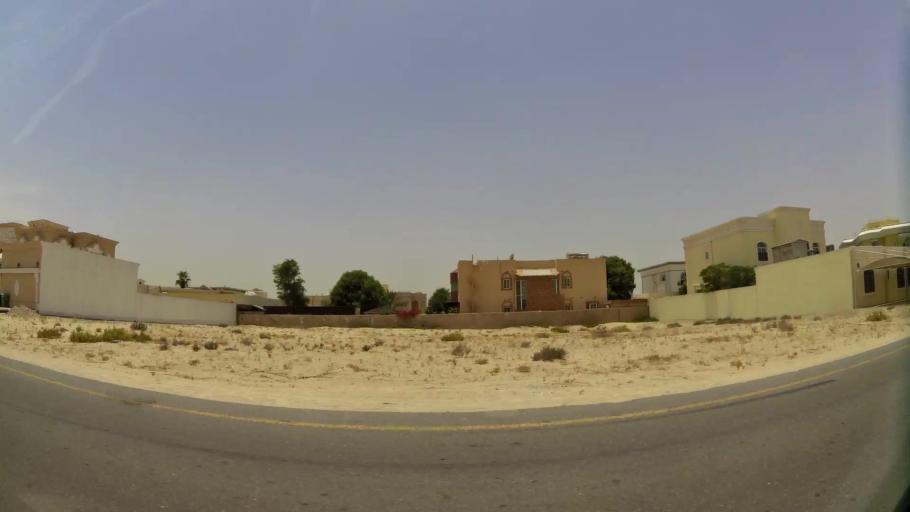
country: AE
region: Ash Shariqah
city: Sharjah
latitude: 25.2467
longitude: 55.4594
